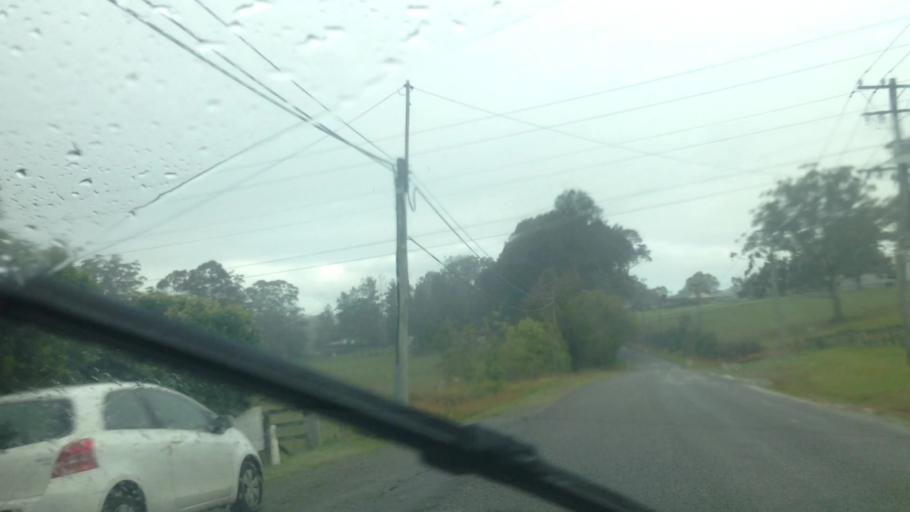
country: AU
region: New South Wales
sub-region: Wyong Shire
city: Little Jilliby
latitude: -33.1978
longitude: 151.3610
